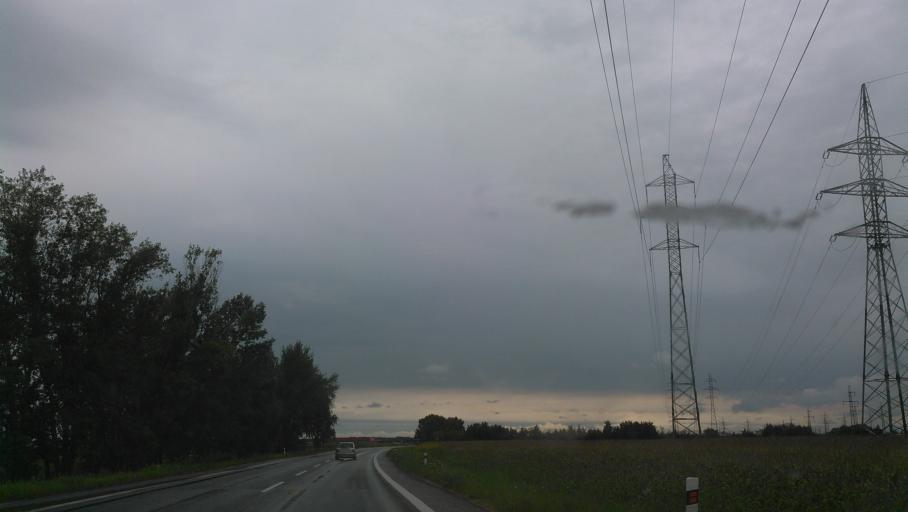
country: SK
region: Trnavsky
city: Dunajska Streda
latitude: 47.9809
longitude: 17.5912
